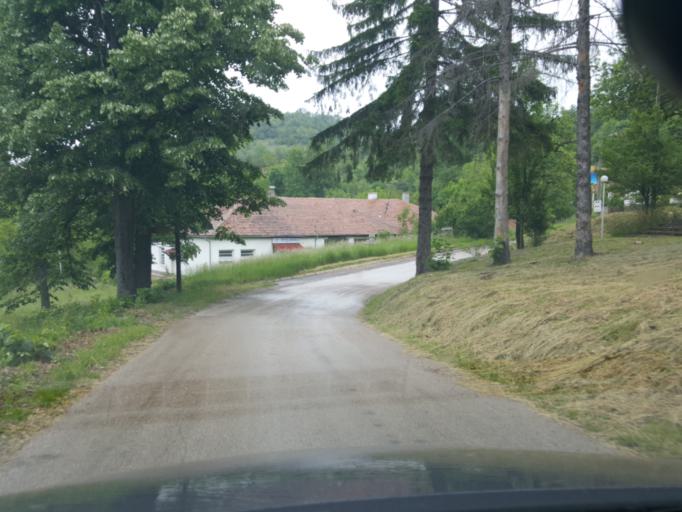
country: RS
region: Central Serbia
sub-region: Zajecarski Okrug
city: Boljevac
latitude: 43.7712
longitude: 21.9338
